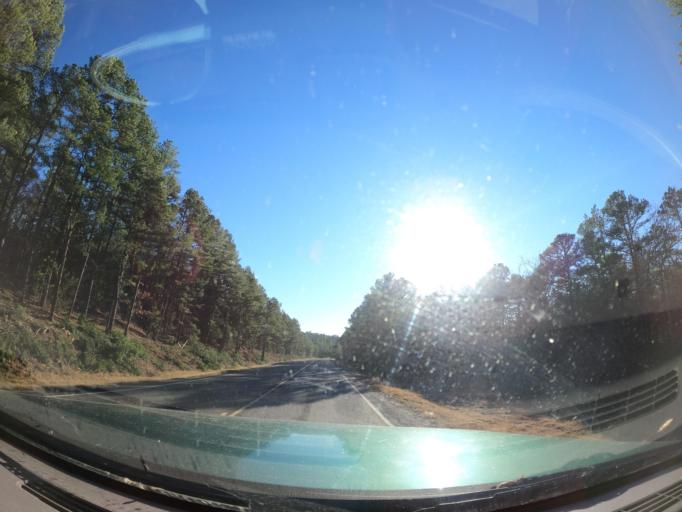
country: US
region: Oklahoma
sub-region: Latimer County
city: Wilburton
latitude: 34.9885
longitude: -95.3523
